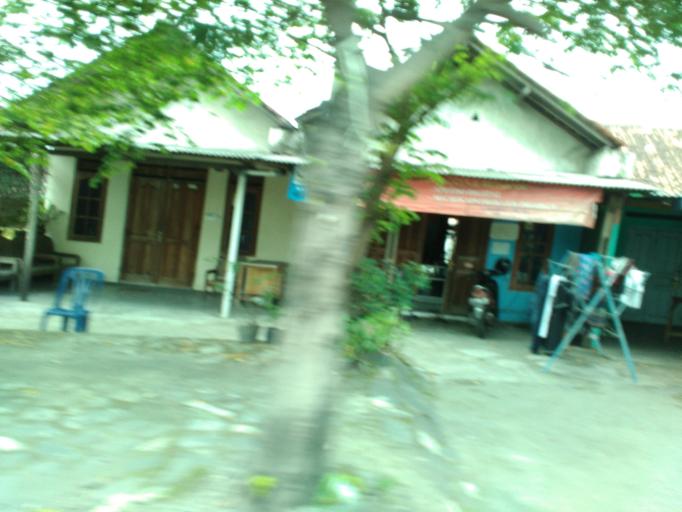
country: ID
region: Central Java
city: Klaten
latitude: -7.6879
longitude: 110.6315
